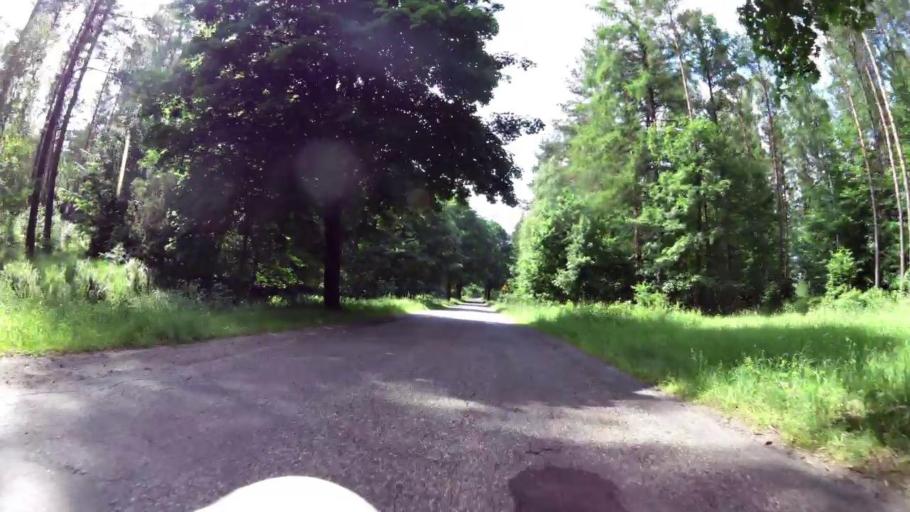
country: PL
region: West Pomeranian Voivodeship
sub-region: Powiat szczecinecki
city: Bialy Bor
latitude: 53.9557
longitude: 16.7521
